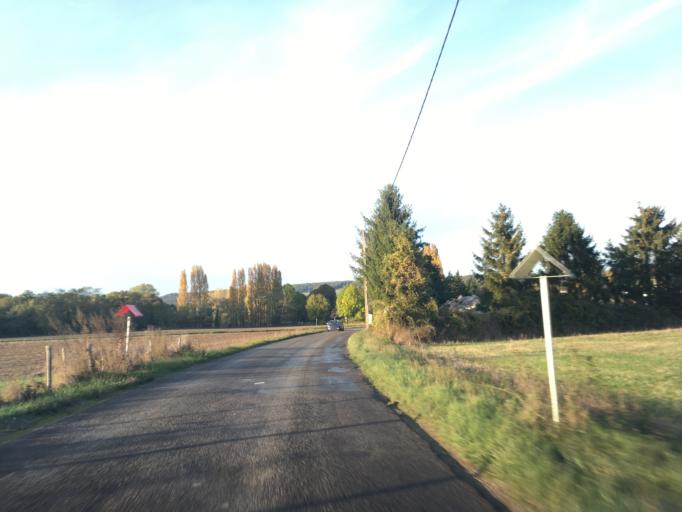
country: FR
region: Haute-Normandie
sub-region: Departement de l'Eure
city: Heudreville-sur-Eure
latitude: 49.1214
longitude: 1.2150
